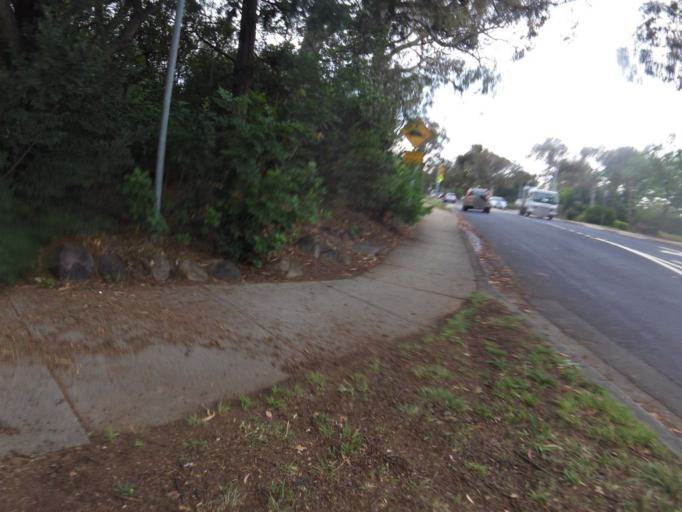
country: AU
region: Australian Capital Territory
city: Forrest
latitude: -35.3426
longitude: 149.1384
